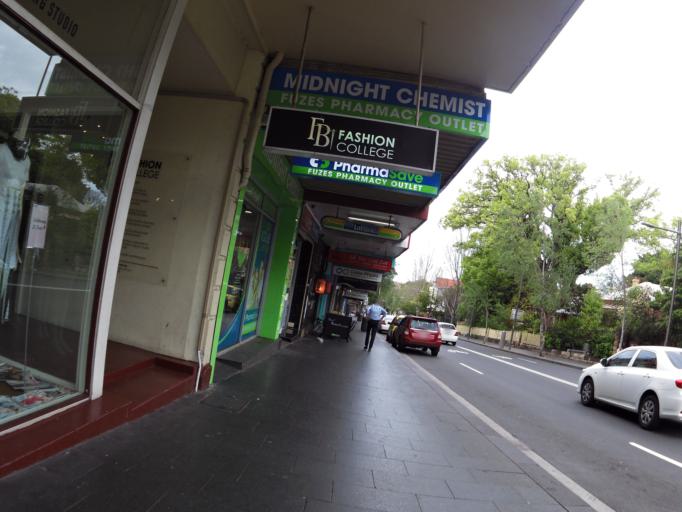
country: AU
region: New South Wales
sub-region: City of Sydney
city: Chippendale
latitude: -33.8813
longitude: 151.1885
